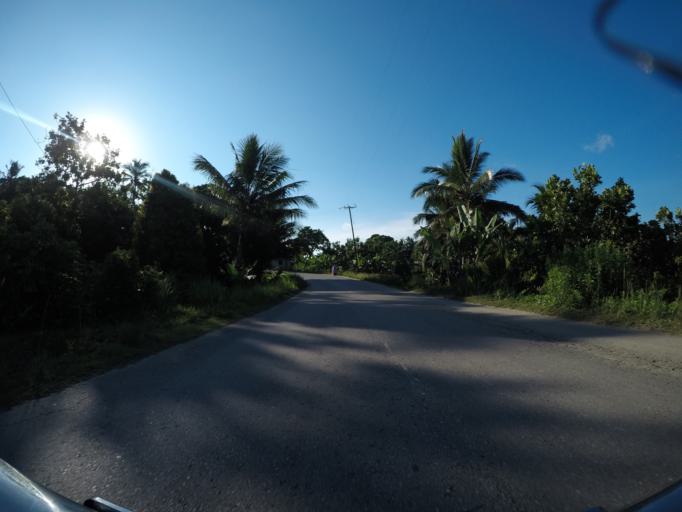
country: TZ
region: Pemba South
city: Mtambile
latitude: -5.3313
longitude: 39.7320
